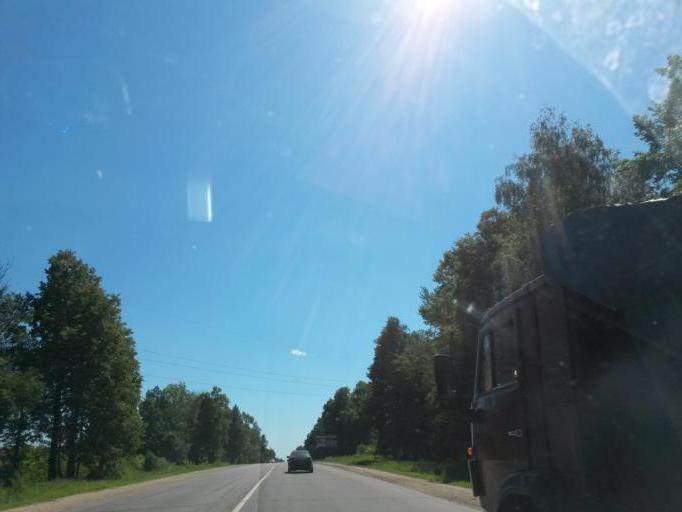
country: RU
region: Moskovskaya
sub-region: Chekhovskiy Rayon
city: Chekhov
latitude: 55.1270
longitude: 37.4508
